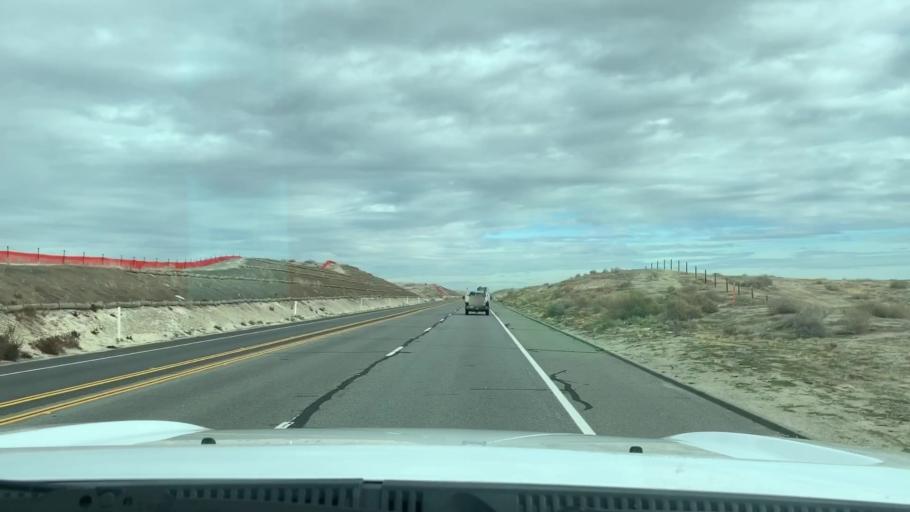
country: US
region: California
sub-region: Kern County
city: Ford City
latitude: 35.2456
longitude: -119.3479
